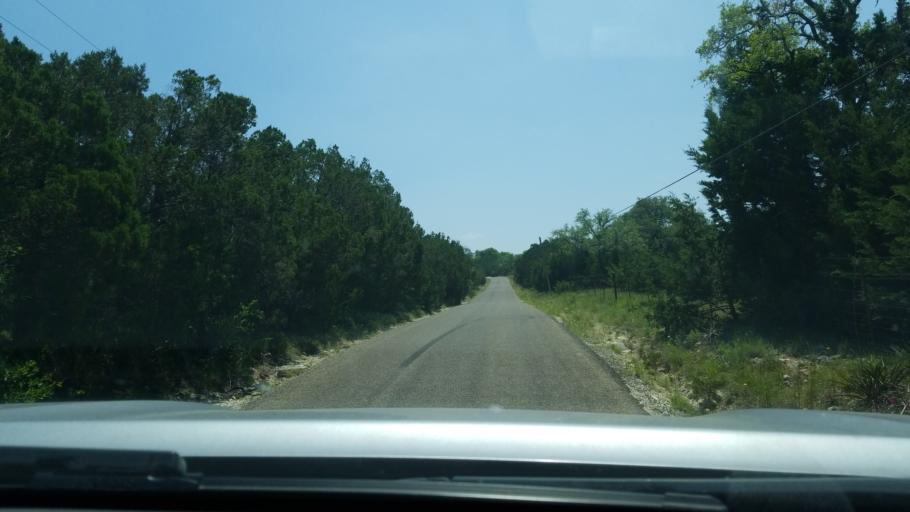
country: US
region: Texas
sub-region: Blanco County
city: Blanco
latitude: 30.0837
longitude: -98.4004
